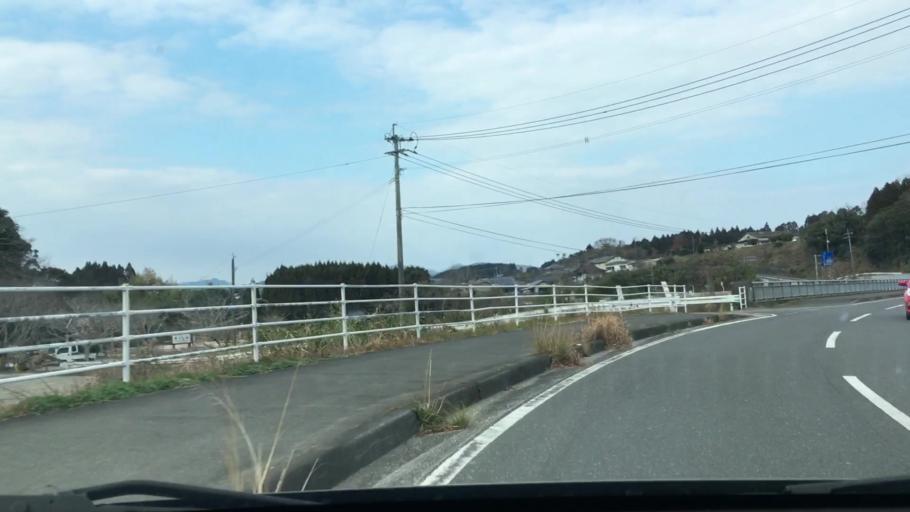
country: JP
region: Miyazaki
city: Kushima
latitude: 31.4990
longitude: 131.2382
